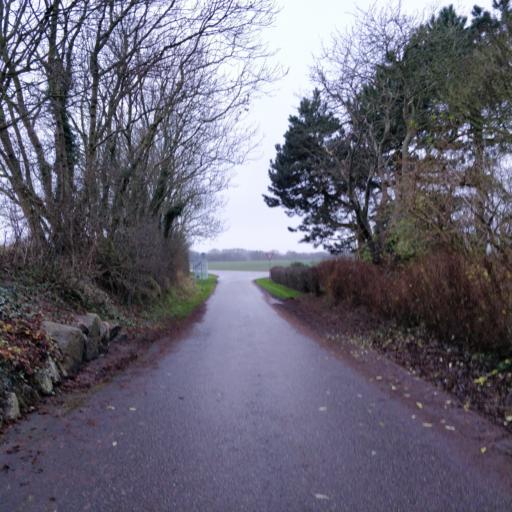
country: DK
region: South Denmark
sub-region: Sonderborg Kommune
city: Guderup
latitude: 54.9736
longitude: 9.9393
